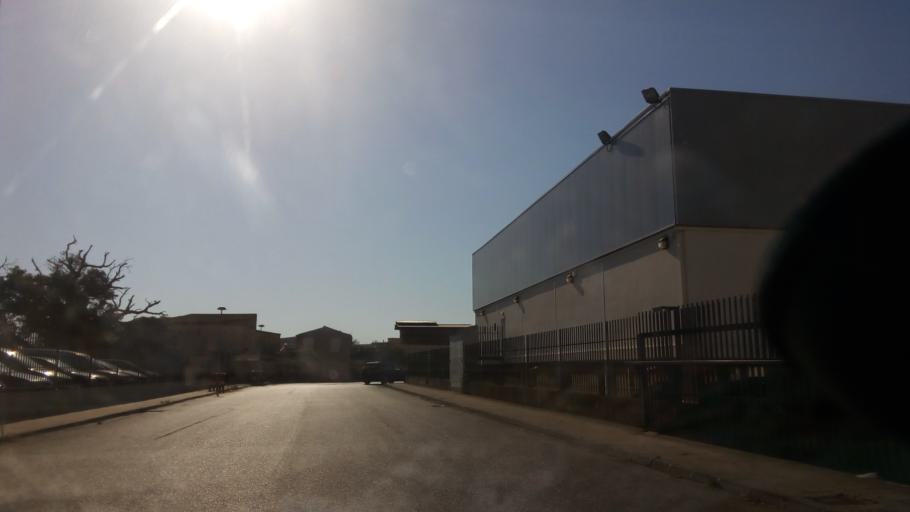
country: ES
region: Balearic Islands
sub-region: Illes Balears
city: Manacor
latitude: 39.5735
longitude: 3.1939
